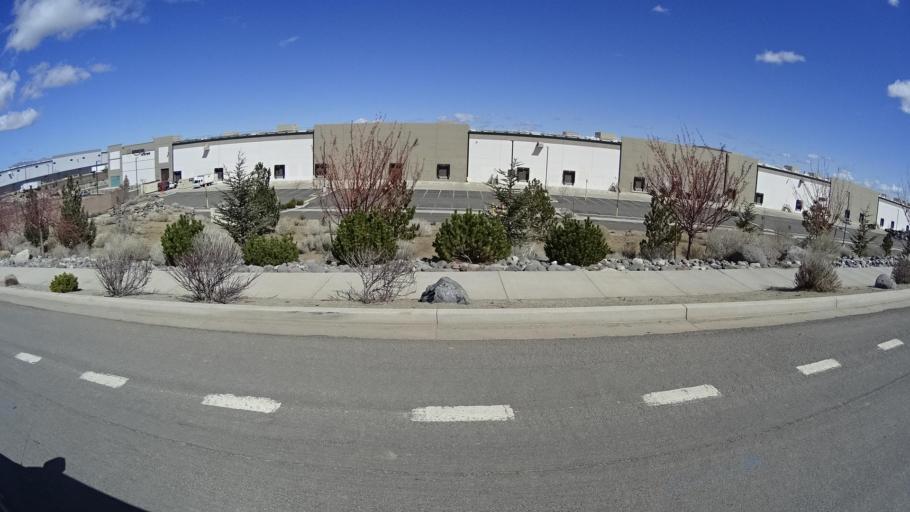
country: US
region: Nevada
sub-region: Washoe County
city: Golden Valley
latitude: 39.6026
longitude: -119.8501
